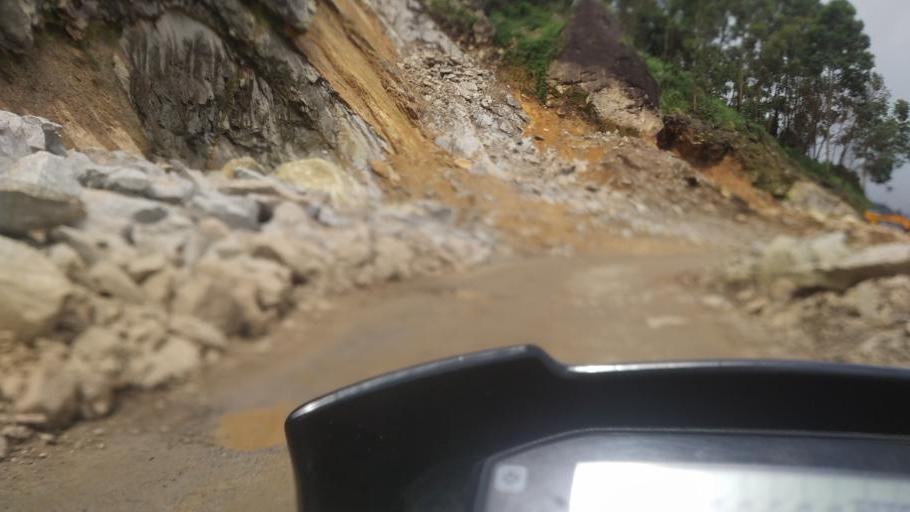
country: IN
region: Kerala
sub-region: Idukki
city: Munnar
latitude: 10.0371
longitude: 77.1307
